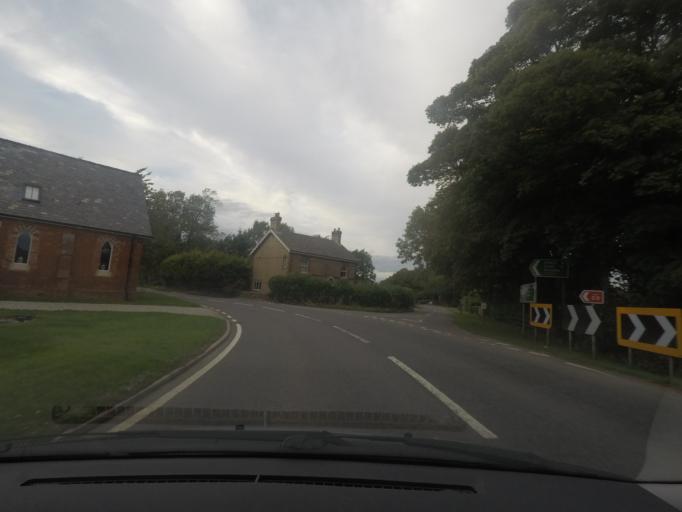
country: GB
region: England
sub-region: Lincolnshire
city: Alford
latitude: 53.2284
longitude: 0.1275
